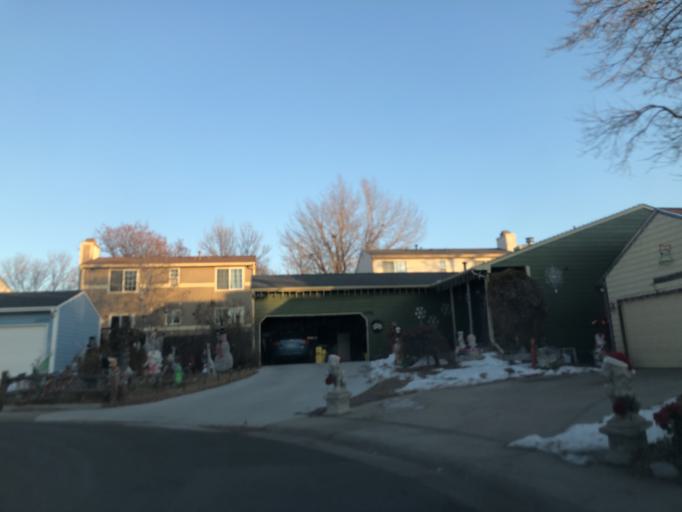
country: US
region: Colorado
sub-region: Adams County
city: Aurora
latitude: 39.7052
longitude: -104.8039
